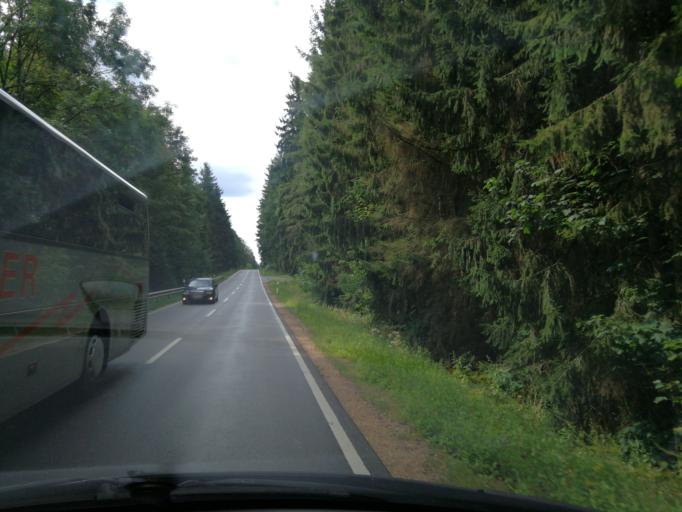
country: DE
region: Bavaria
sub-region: Upper Palatinate
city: Wiesent
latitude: 49.0258
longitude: 12.3740
